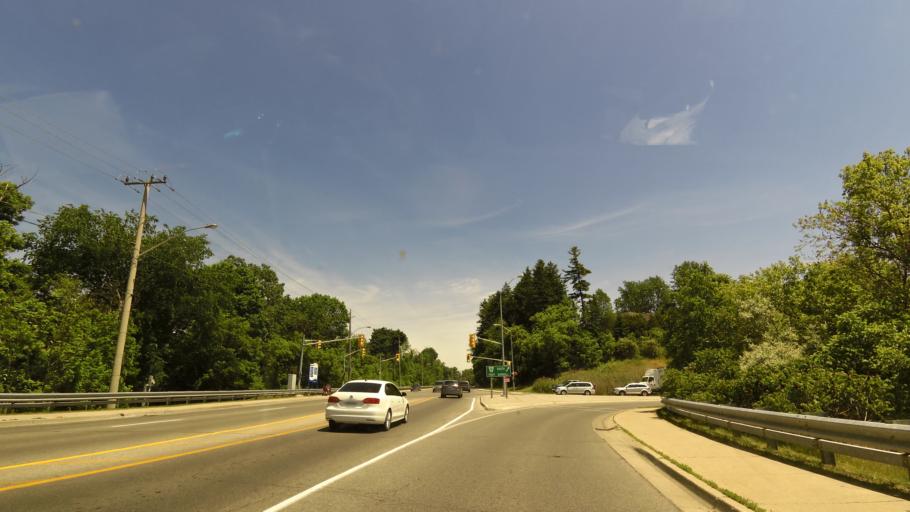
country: CA
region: Ontario
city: Ingersoll
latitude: 42.8601
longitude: -80.7190
